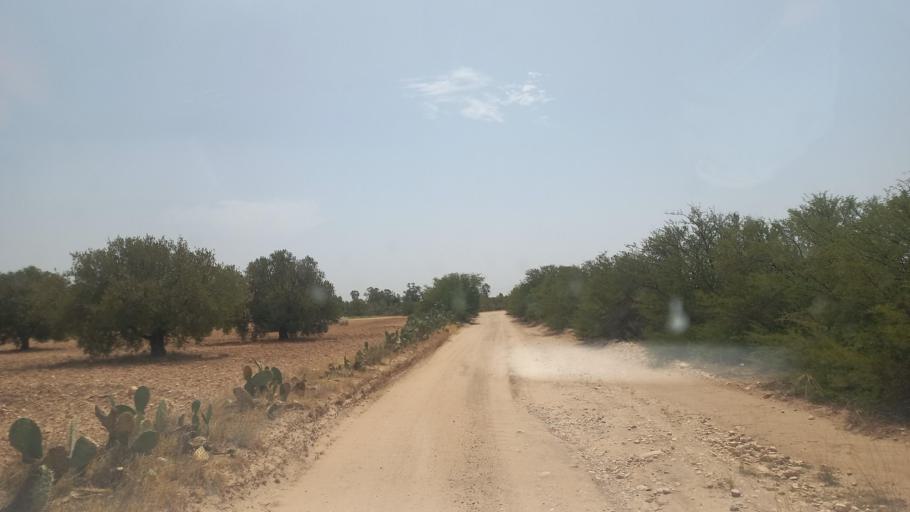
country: TN
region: Al Qasrayn
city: Kasserine
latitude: 35.2543
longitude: 9.0074
